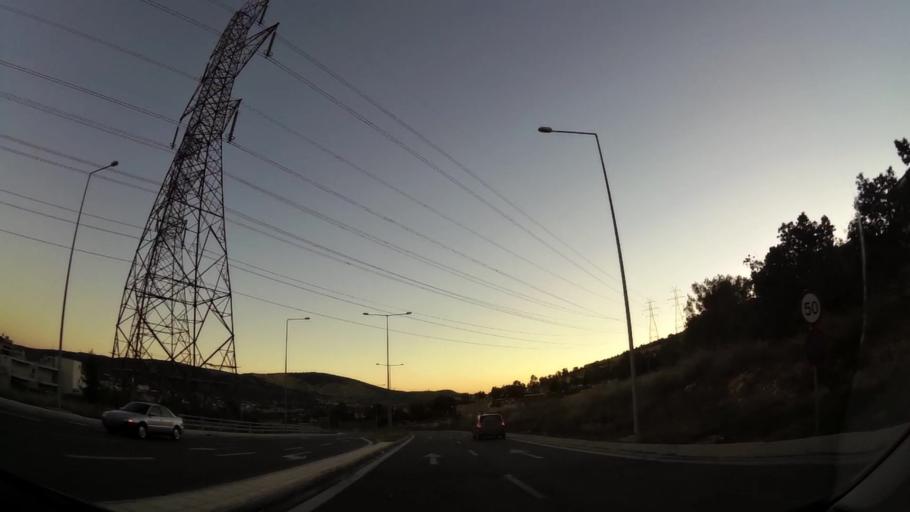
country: GR
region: Attica
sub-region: Nomarchia Dytikis Attikis
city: Ano Liosia
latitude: 38.0871
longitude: 23.6821
